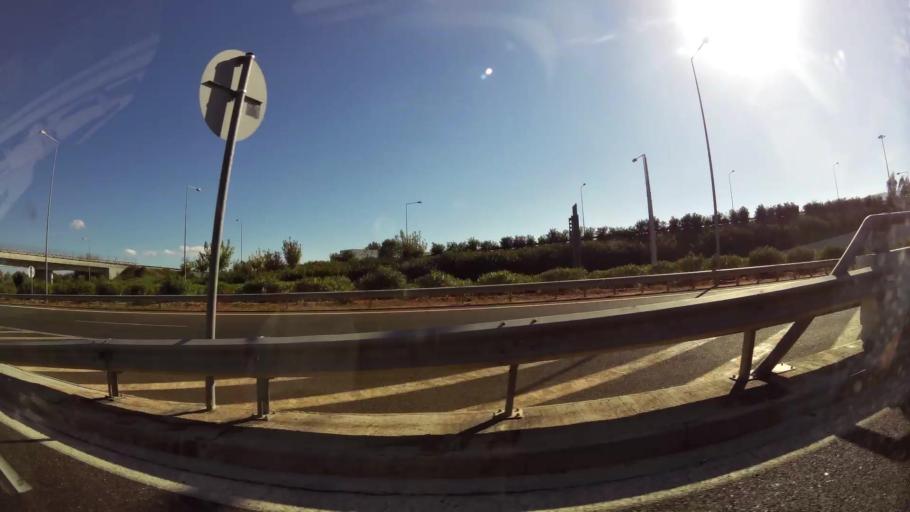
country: GR
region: Attica
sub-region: Nomarchia Anatolikis Attikis
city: Pallini
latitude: 37.9949
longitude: 23.8747
